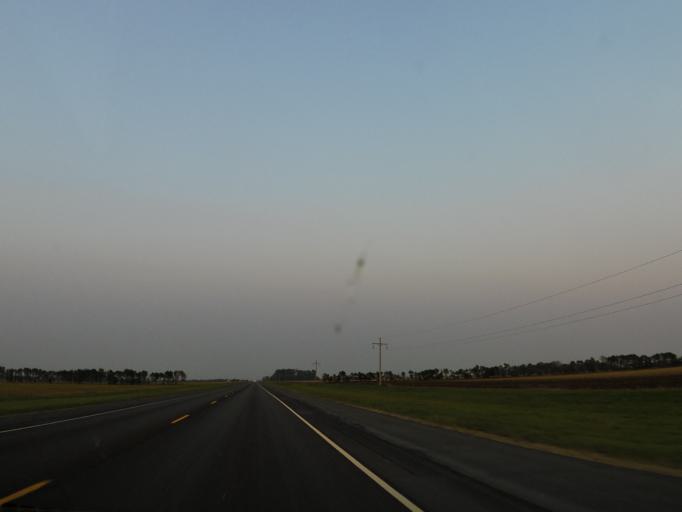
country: US
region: North Dakota
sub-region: Walsh County
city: Grafton
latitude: 48.4127
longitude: -97.5511
